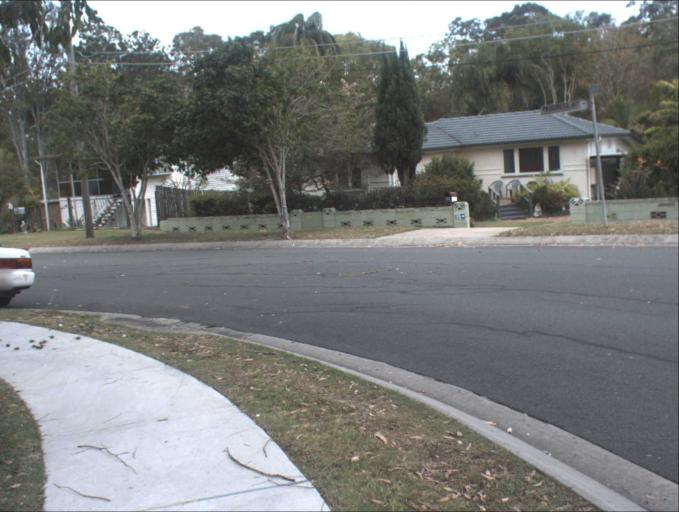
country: AU
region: Queensland
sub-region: Logan
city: Woodridge
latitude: -27.6348
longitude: 153.0960
